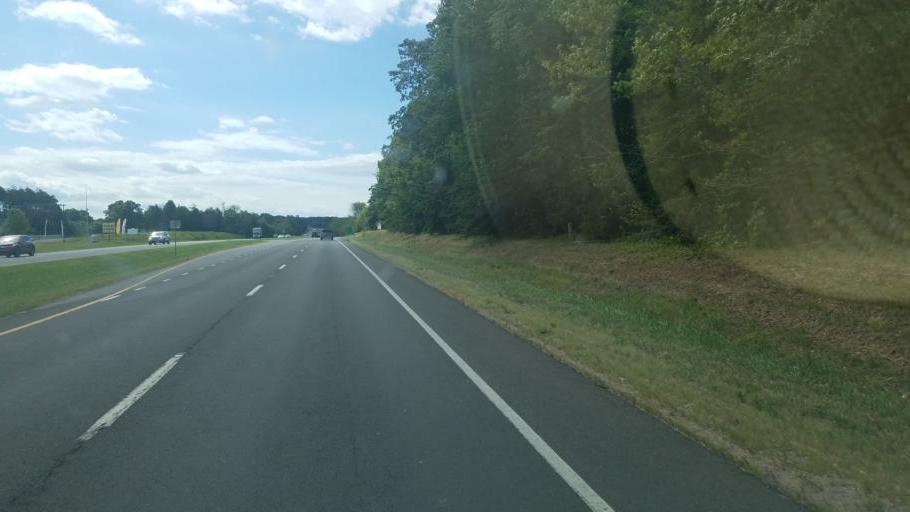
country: US
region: Virginia
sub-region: Fauquier County
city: Bealeton
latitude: 38.5226
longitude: -77.7240
